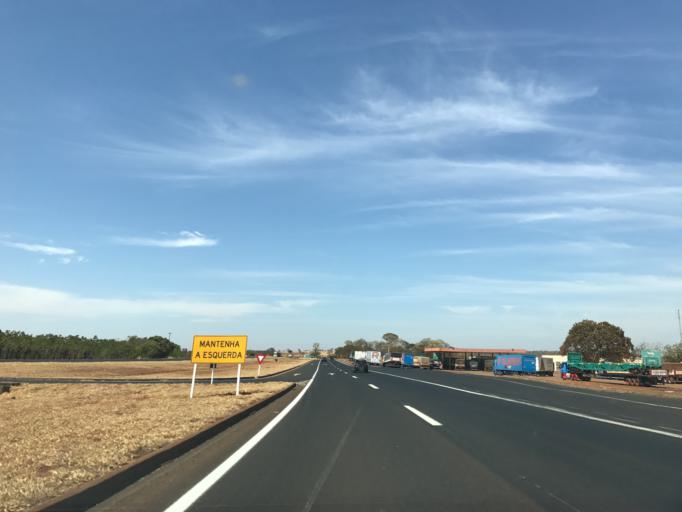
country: BR
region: Minas Gerais
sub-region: Monte Alegre De Minas
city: Monte Alegre de Minas
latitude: -18.8151
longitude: -49.0872
